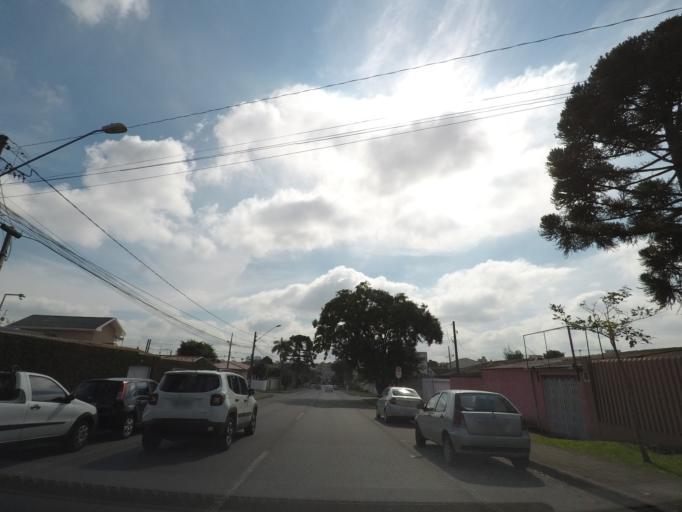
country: BR
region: Parana
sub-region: Curitiba
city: Curitiba
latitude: -25.4818
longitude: -49.2704
